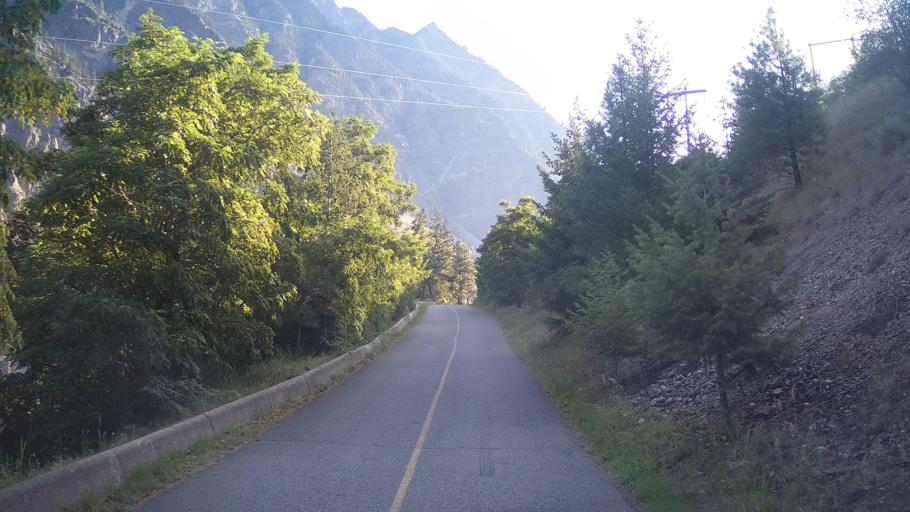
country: CA
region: British Columbia
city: Lillooet
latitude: 50.6654
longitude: -121.9899
